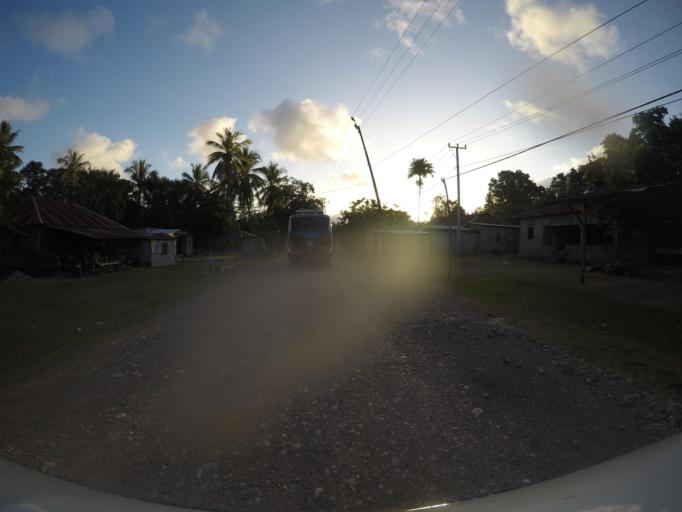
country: TL
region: Baucau
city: Venilale
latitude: -8.7480
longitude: 126.7075
